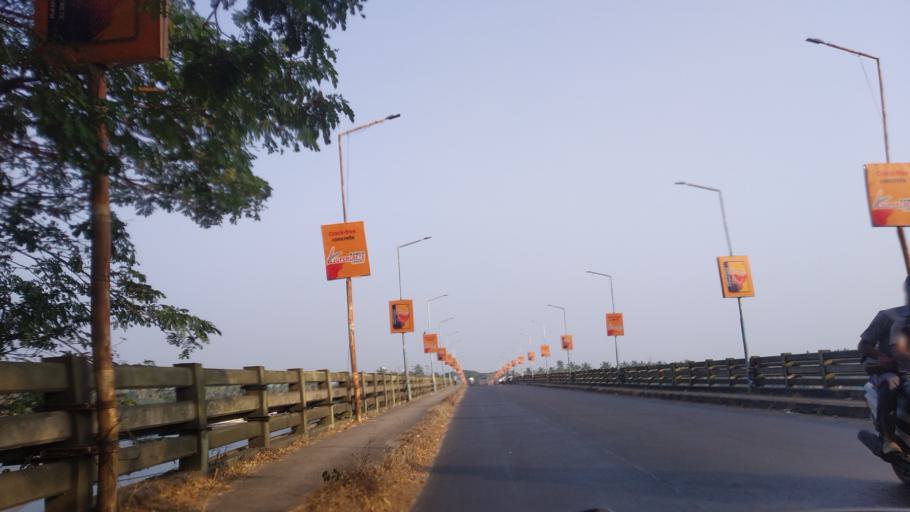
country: IN
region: Kerala
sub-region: Thrissur District
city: Kodungallur
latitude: 10.1924
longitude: 76.2013
